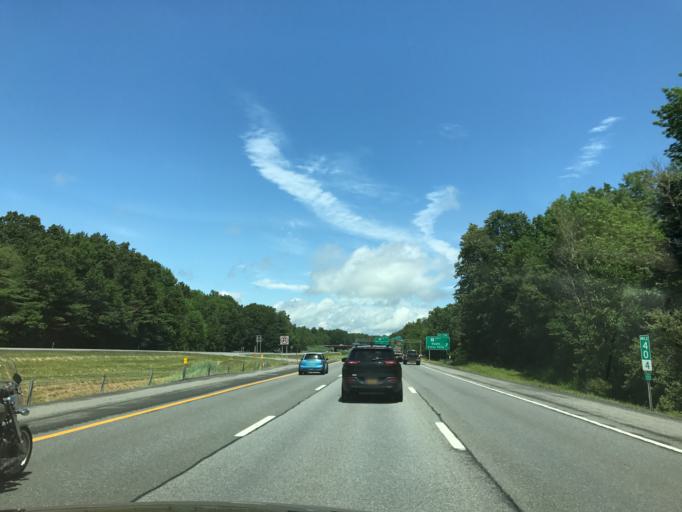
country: US
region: New York
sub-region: Warren County
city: West Glens Falls
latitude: 43.2294
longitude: -73.6918
